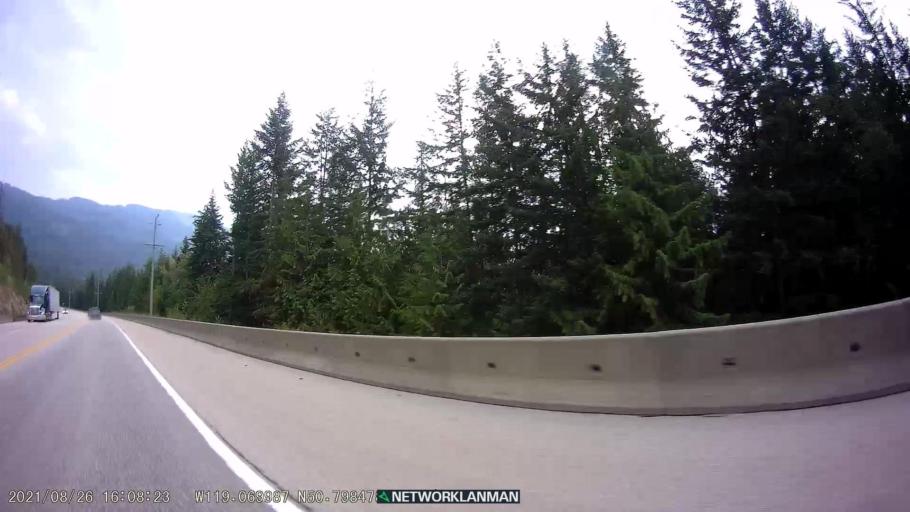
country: CA
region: British Columbia
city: Sicamous
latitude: 50.7985
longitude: -119.0697
